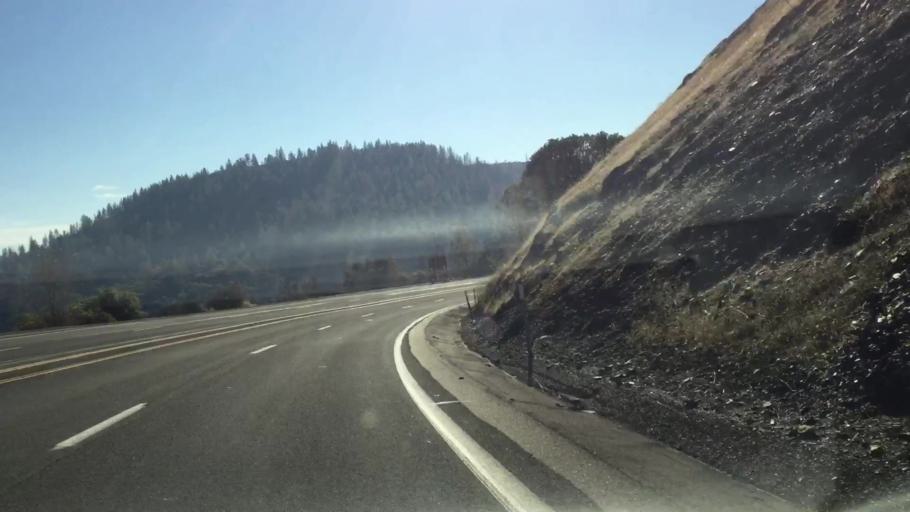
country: US
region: California
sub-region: Butte County
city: Berry Creek
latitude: 39.6704
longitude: -121.5262
